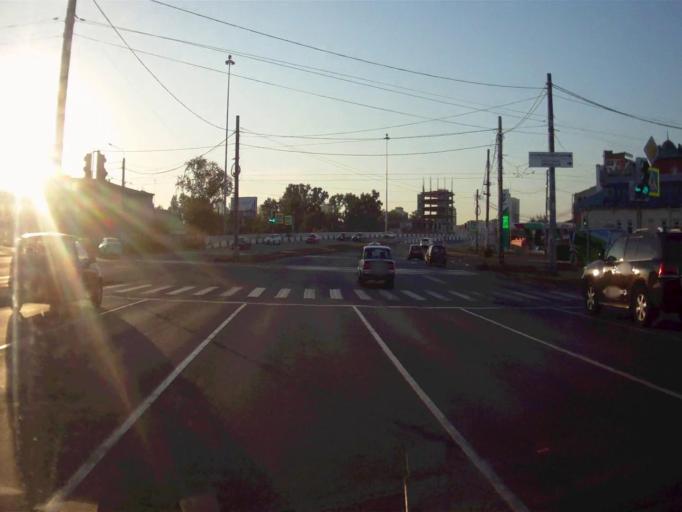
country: RU
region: Chelyabinsk
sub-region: Gorod Chelyabinsk
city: Chelyabinsk
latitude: 55.1683
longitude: 61.4138
